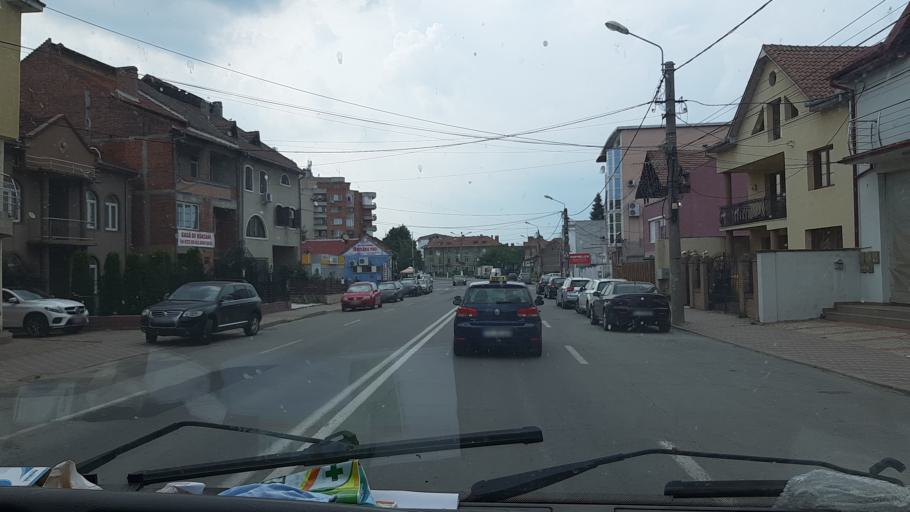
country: RO
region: Timis
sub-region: Municipiul Lugoj
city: Lugoj
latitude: 45.6959
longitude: 21.9002
